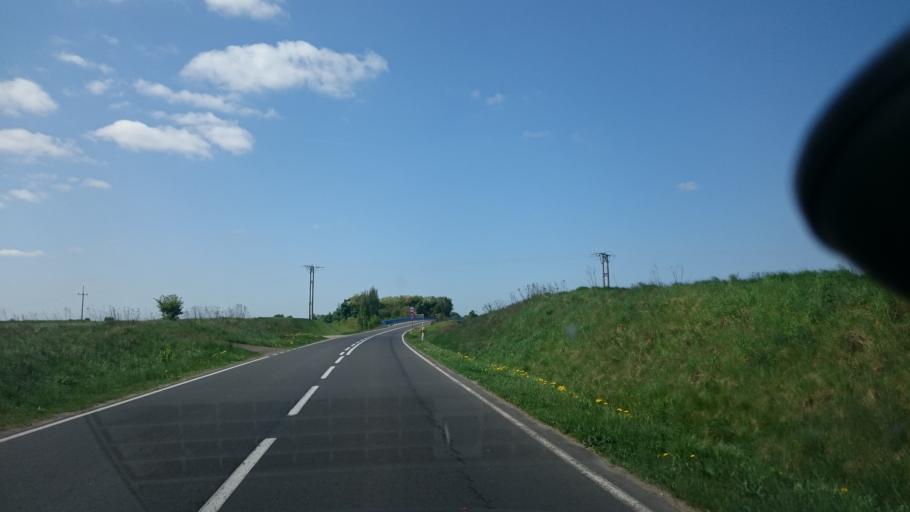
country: PL
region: Kujawsko-Pomorskie
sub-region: Powiat swiecki
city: Warlubie
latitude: 53.5961
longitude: 18.6198
